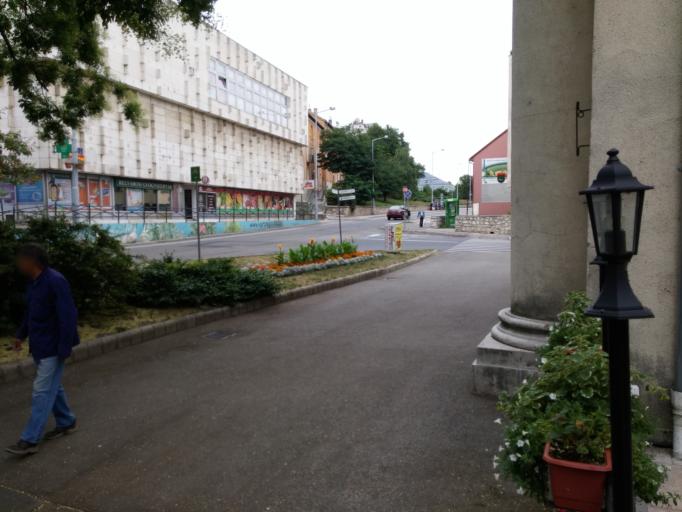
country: HU
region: Veszprem
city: Varpalota
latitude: 47.2007
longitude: 18.1408
